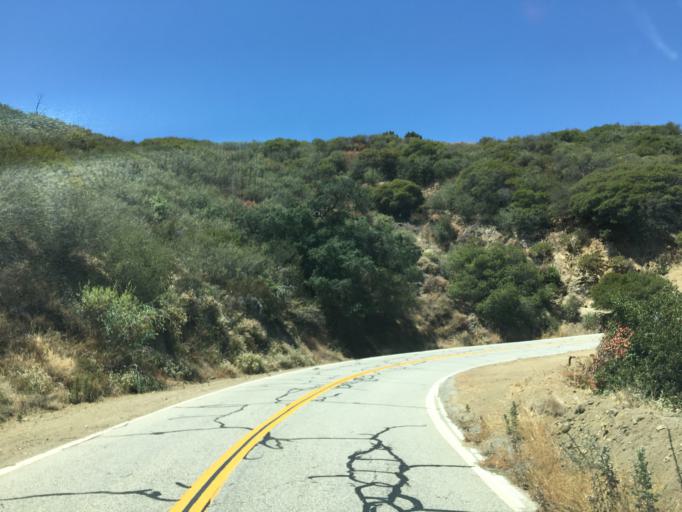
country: US
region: California
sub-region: Los Angeles County
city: Glendora
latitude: 34.1748
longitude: -117.8490
